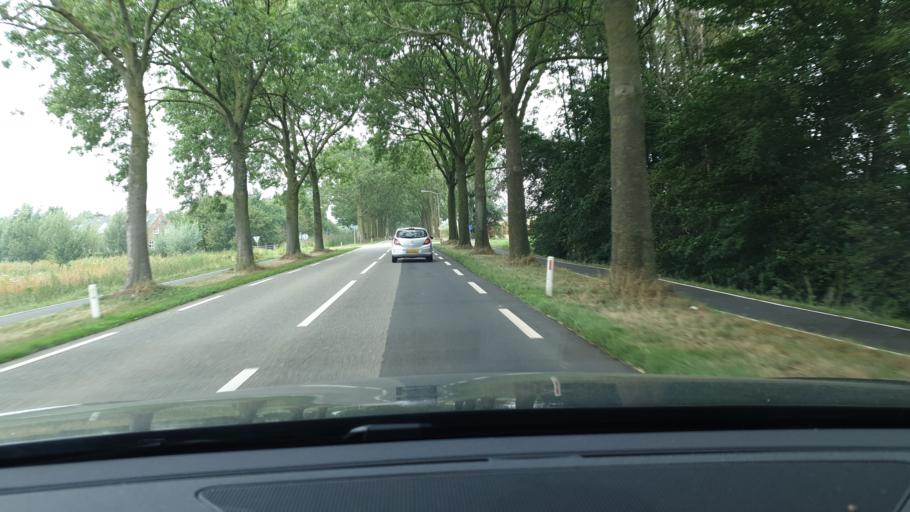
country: NL
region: Gelderland
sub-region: Gemeente Maasdriel
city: Heerewaarden
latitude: 51.7574
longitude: 5.3649
